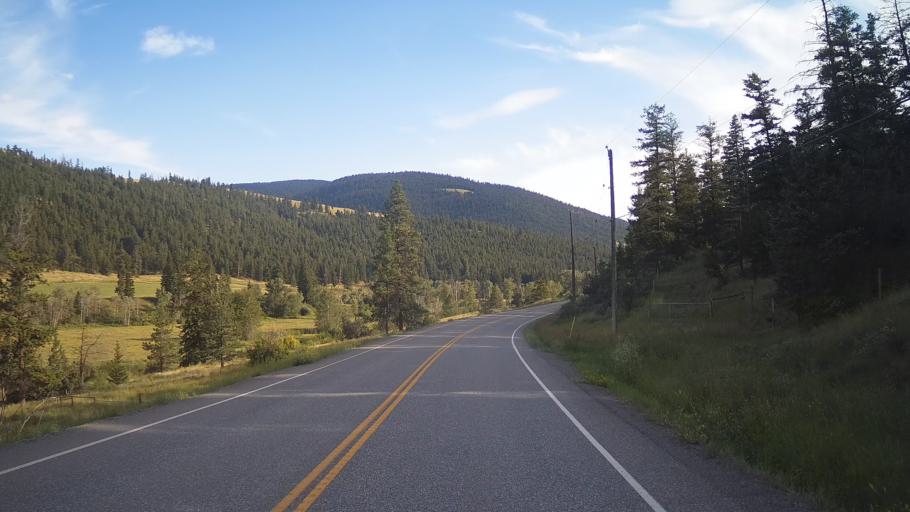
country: CA
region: British Columbia
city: Cache Creek
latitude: 50.8428
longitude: -121.5412
